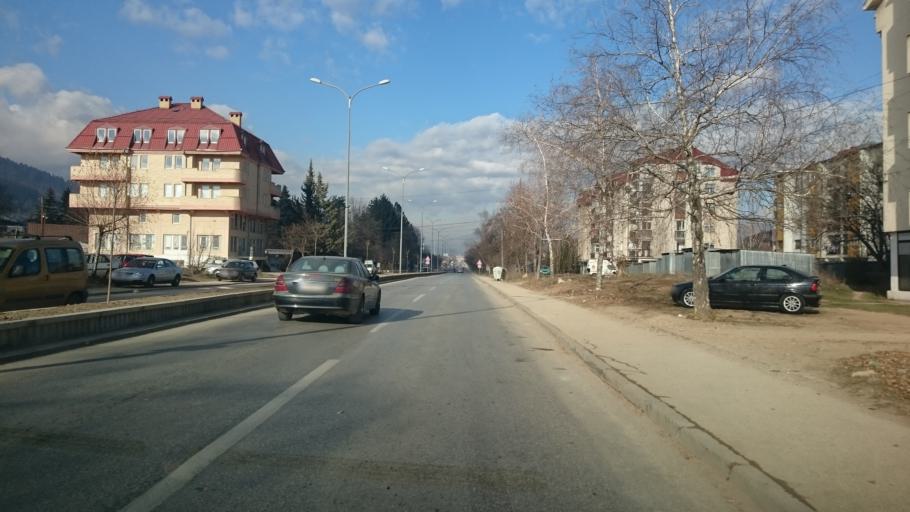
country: MK
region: Kicevo
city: Kicevo
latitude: 41.5041
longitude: 20.9525
